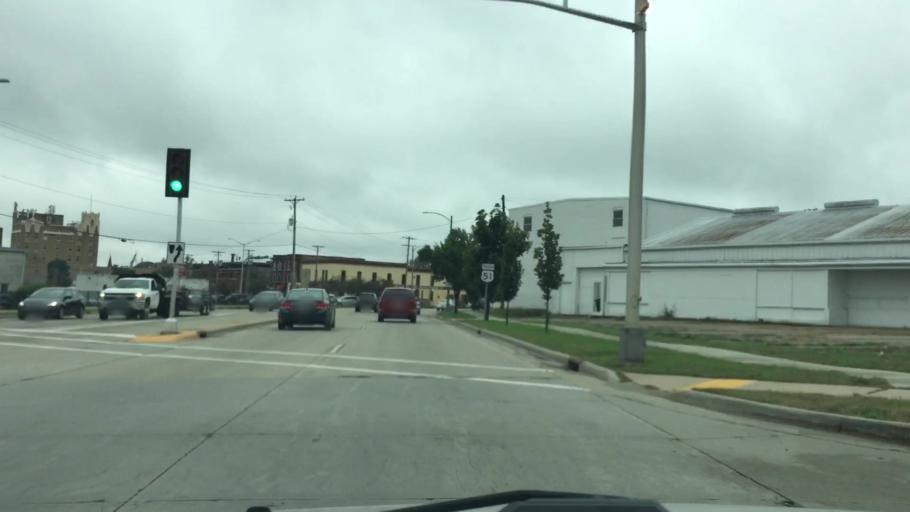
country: US
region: Wisconsin
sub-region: Rock County
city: Janesville
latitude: 42.6834
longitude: -89.0287
